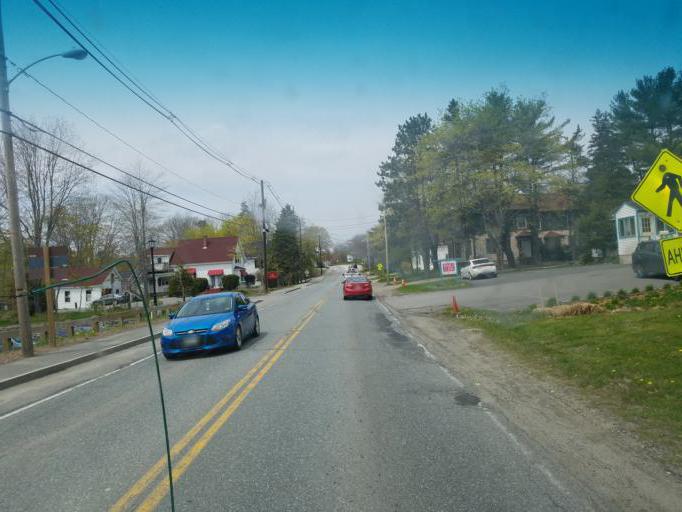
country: US
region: Maine
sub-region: Hancock County
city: Ellsworth
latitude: 44.5476
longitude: -68.4238
